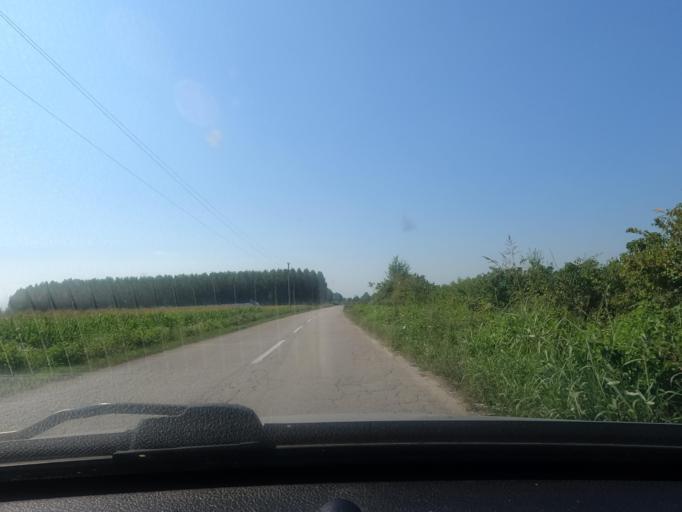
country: RS
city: Kozjak
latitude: 44.5728
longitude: 19.2805
